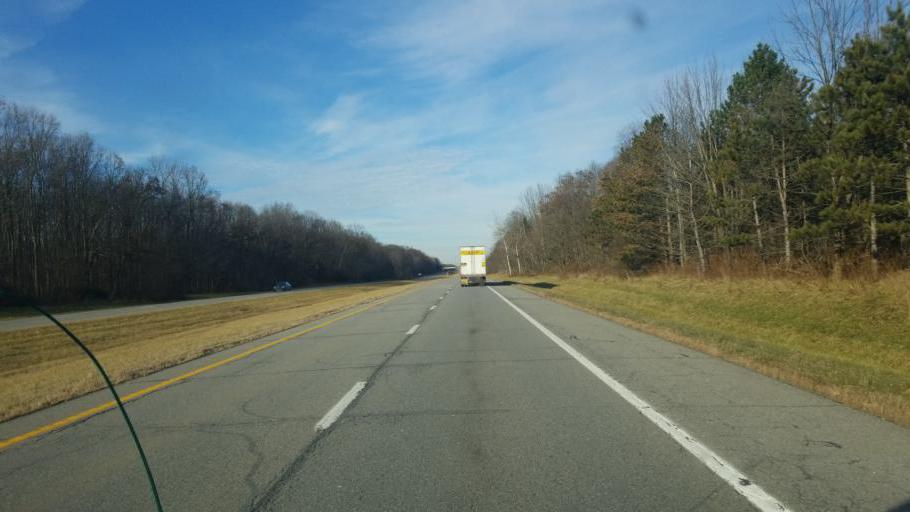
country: US
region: Ohio
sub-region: Ashtabula County
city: Orwell
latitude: 41.4947
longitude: -80.7131
